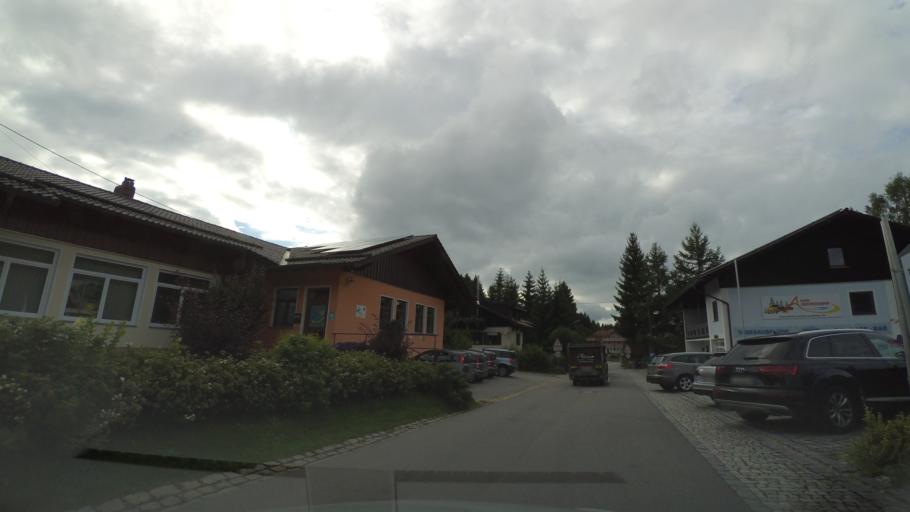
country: DE
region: Bavaria
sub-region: Upper Palatinate
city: Lohberg
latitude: 49.1707
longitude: 13.0907
